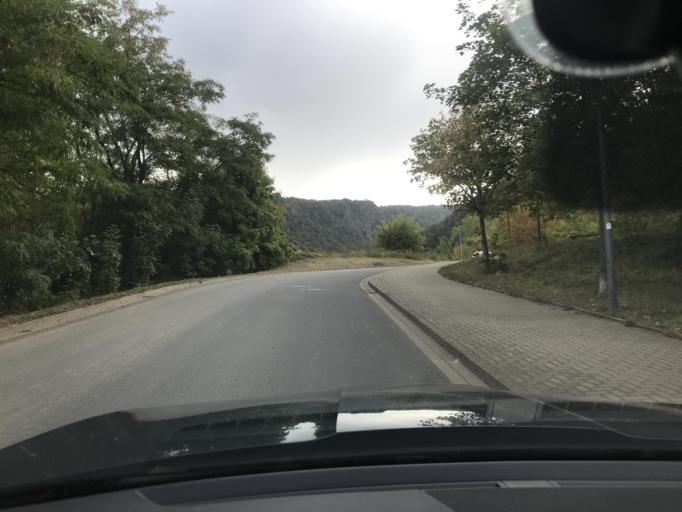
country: DE
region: Saxony-Anhalt
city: Thale
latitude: 51.7493
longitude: 11.0271
